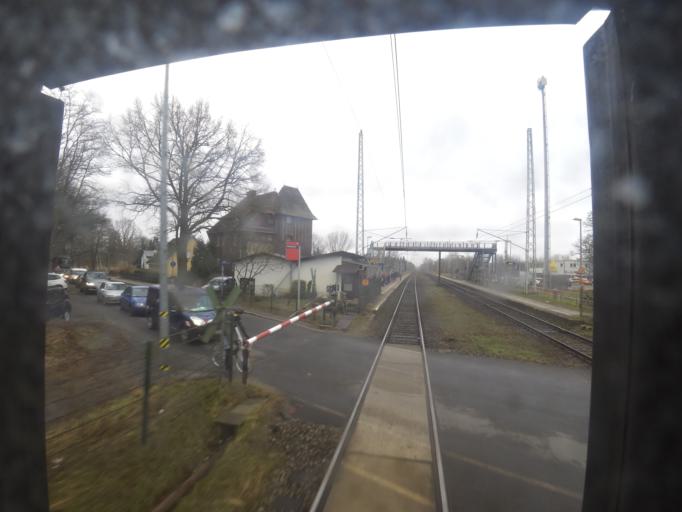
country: DE
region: Brandenburg
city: Zossen
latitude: 52.2378
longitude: 13.4375
